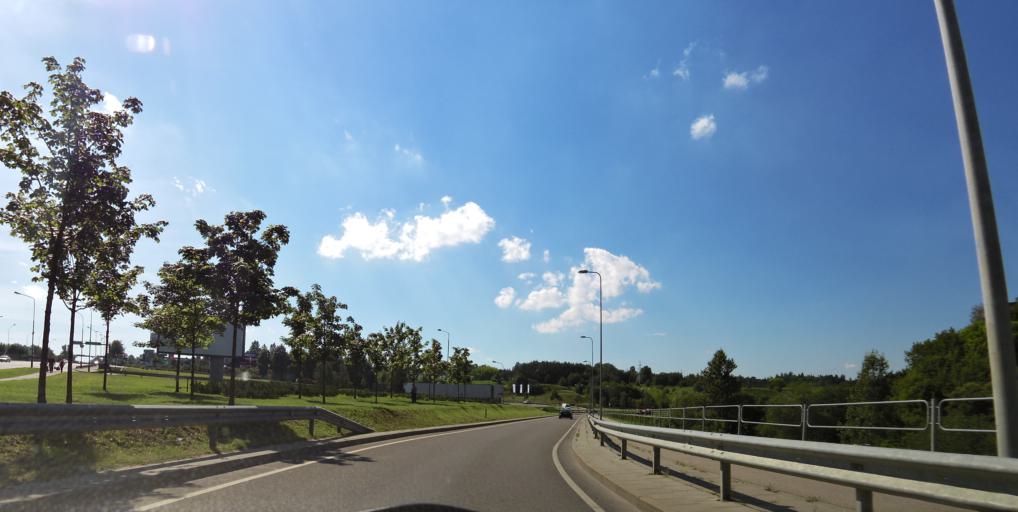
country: LT
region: Vilnius County
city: Naujamiestis
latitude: 54.6579
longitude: 25.2722
